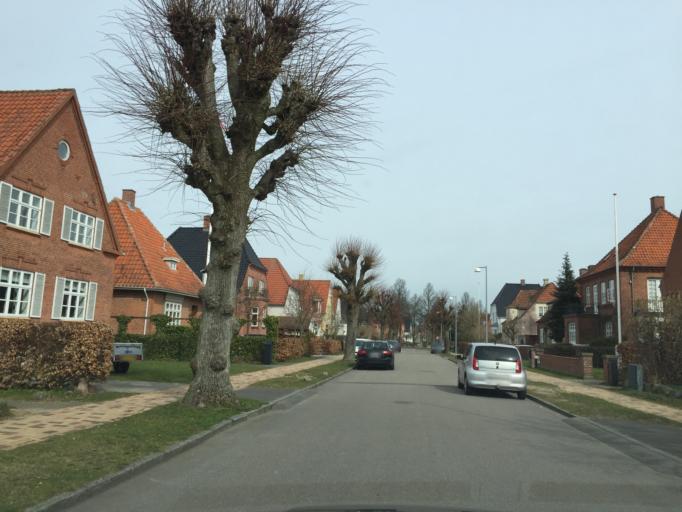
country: DK
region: South Denmark
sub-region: Odense Kommune
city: Odense
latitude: 55.3834
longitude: 10.3809
